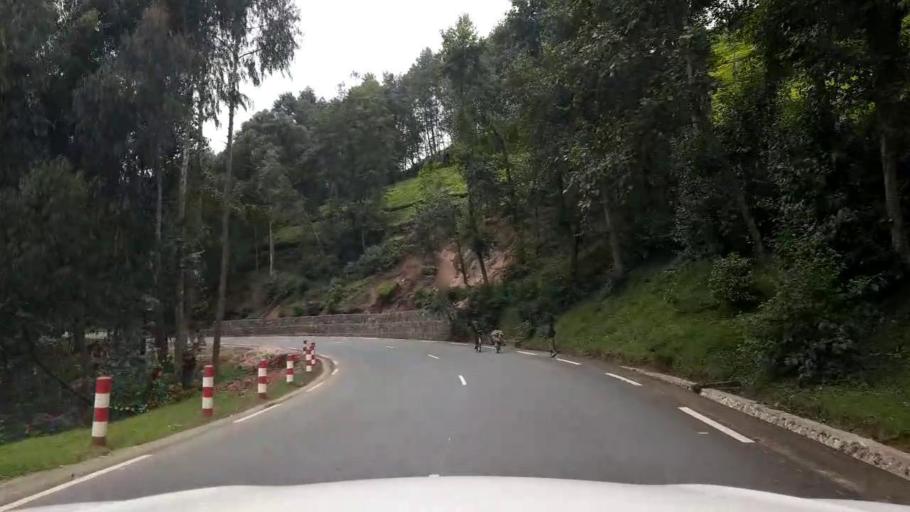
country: RW
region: Northern Province
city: Musanze
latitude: -1.6568
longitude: 29.5095
